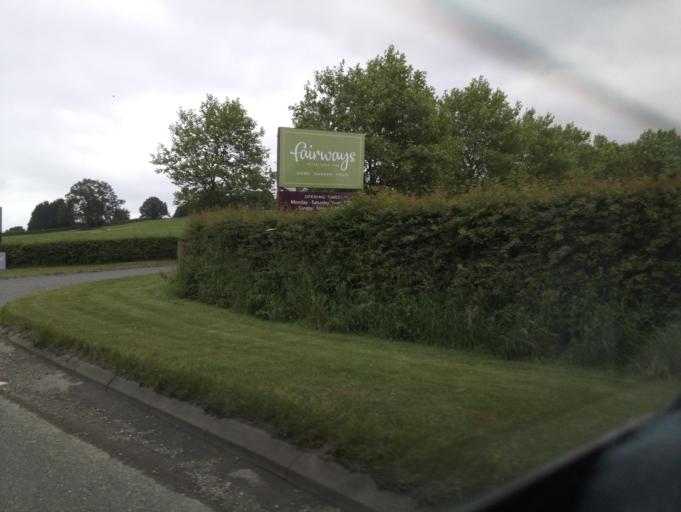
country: GB
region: England
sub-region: Staffordshire
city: Mayfield
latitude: 52.9983
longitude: -1.7507
